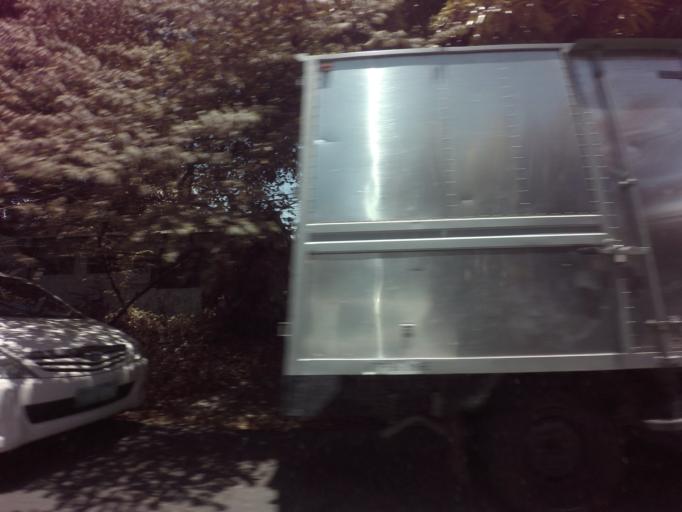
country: PH
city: Sambayanihan People's Village
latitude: 14.4868
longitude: 121.0384
